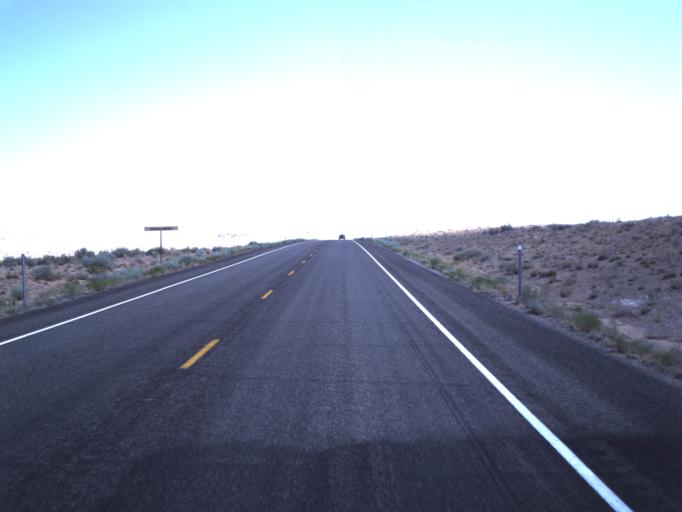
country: US
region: Utah
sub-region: Emery County
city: Ferron
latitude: 38.4634
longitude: -110.6729
